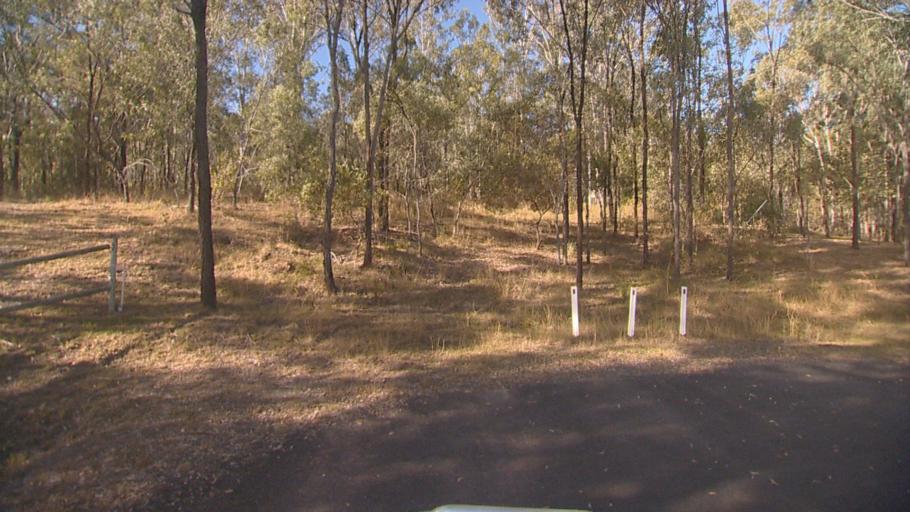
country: AU
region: Queensland
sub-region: Logan
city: Cedar Vale
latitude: -27.8349
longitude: 153.0738
